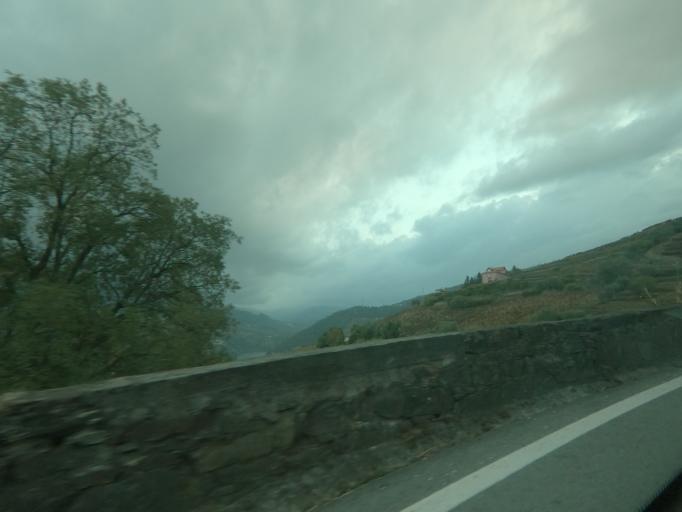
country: PT
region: Vila Real
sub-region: Mesao Frio
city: Mesao Frio
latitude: 41.1588
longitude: -7.8814
